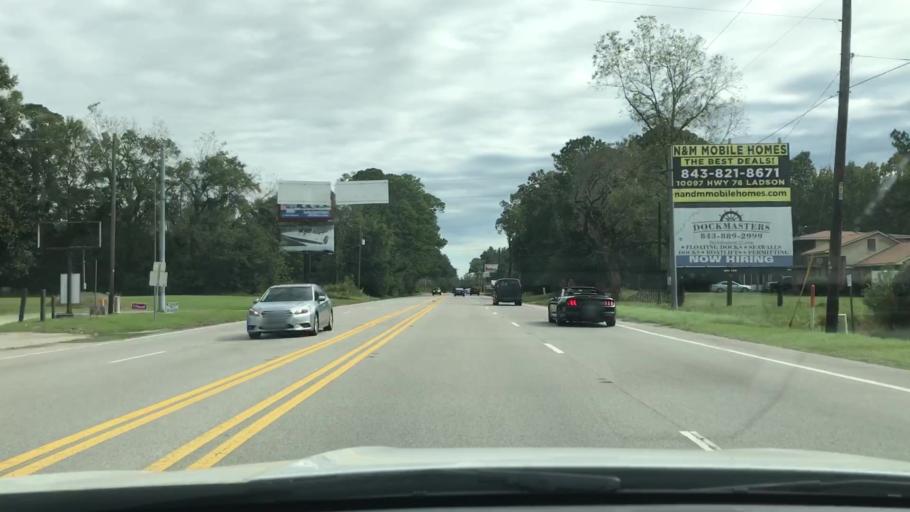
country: US
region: South Carolina
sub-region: Charleston County
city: Ravenel
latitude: 32.7726
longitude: -80.4581
